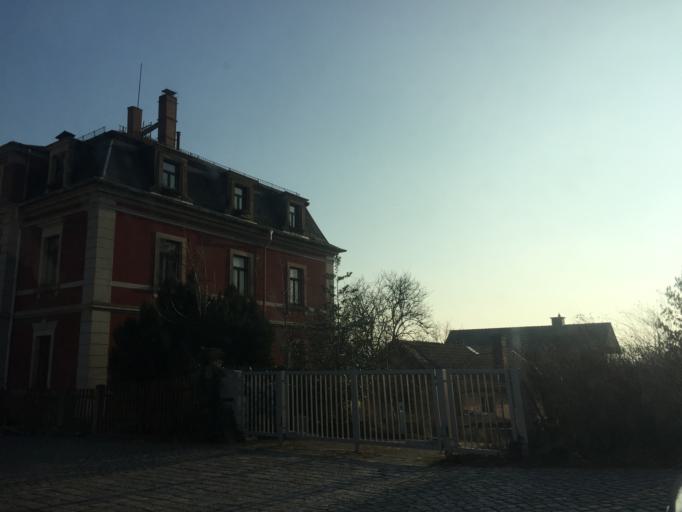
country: DE
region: Saxony
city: Heidenau
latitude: 51.0273
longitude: 13.8489
